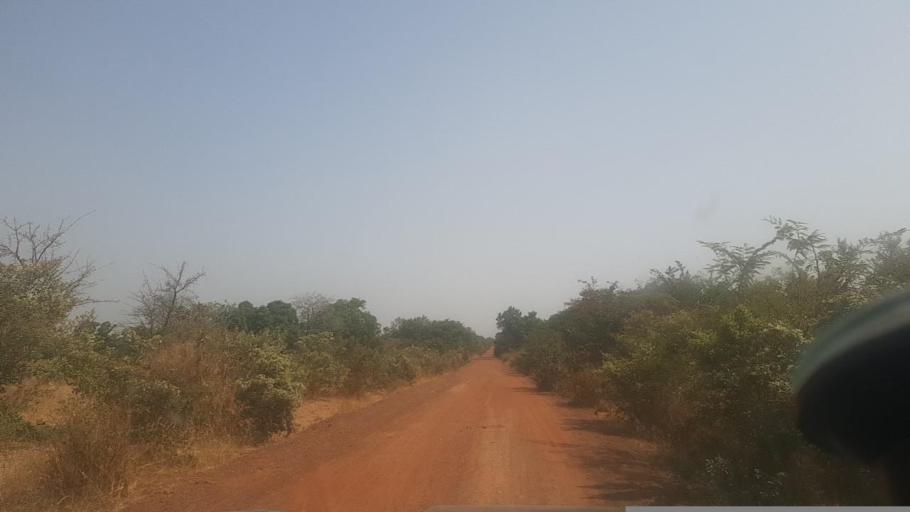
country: ML
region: Segou
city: Bla
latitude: 12.9245
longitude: -6.2683
